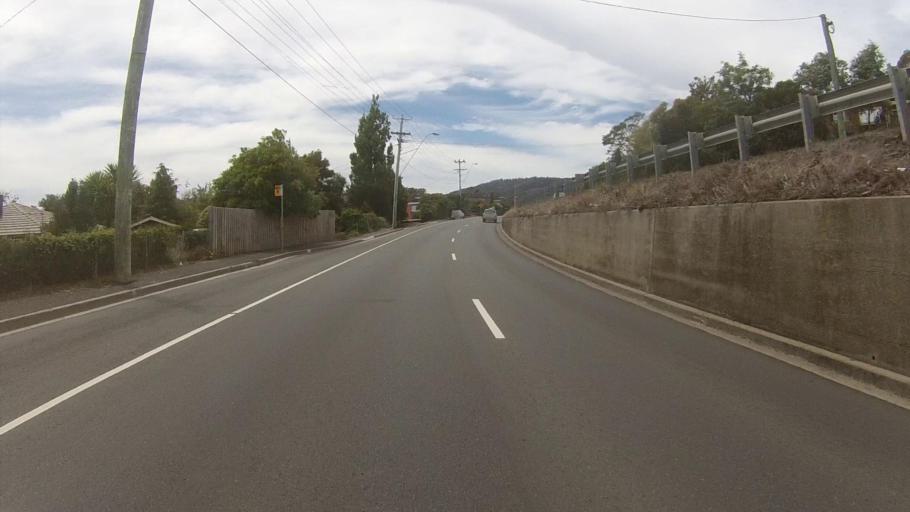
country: AU
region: Tasmania
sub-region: Clarence
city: Lindisfarne
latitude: -42.8537
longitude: 147.3573
